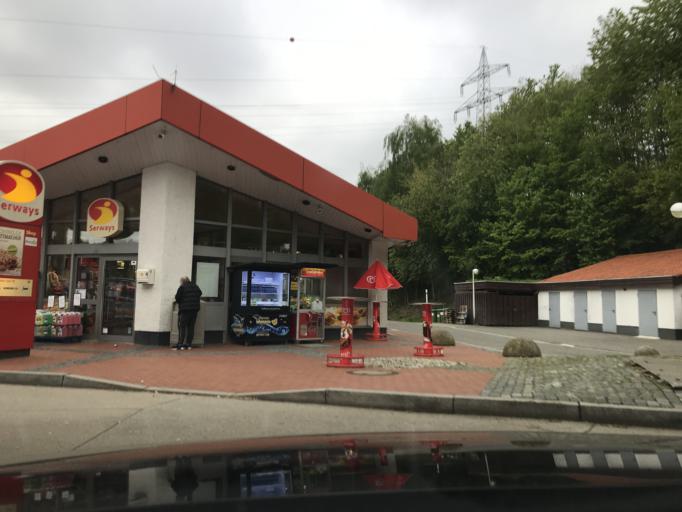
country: DE
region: Bavaria
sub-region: Regierungsbezirk Mittelfranken
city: Greding
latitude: 49.0463
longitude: 11.3365
